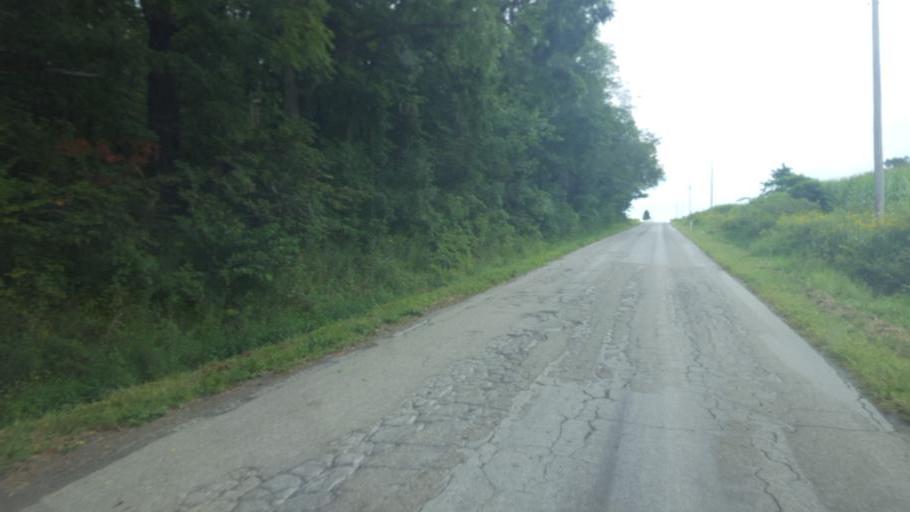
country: US
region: Ohio
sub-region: Richland County
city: Lexington
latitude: 40.6012
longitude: -82.6297
